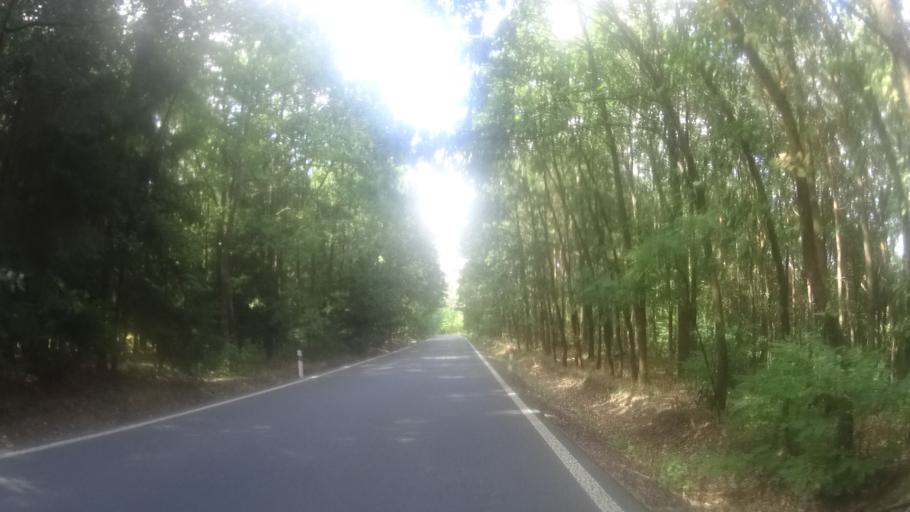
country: CZ
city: Borohradek
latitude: 50.0884
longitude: 16.1069
